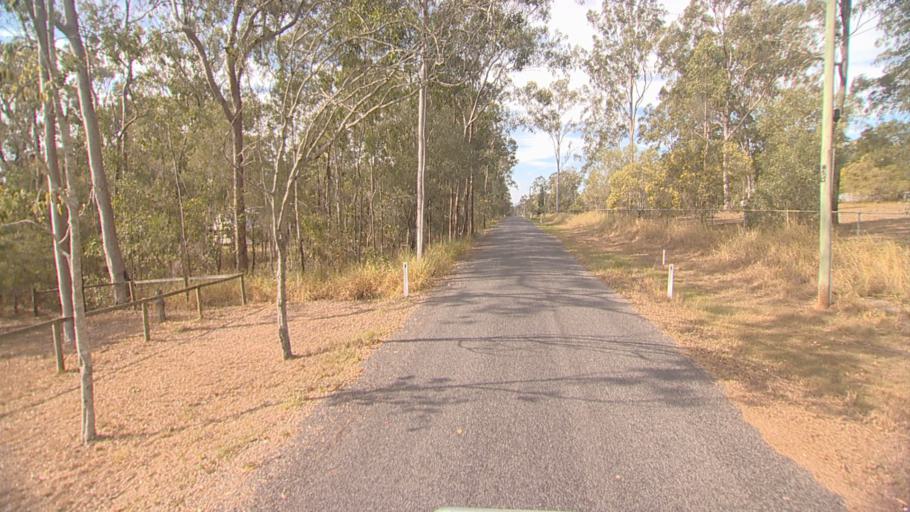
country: AU
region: Queensland
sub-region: Logan
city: North Maclean
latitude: -27.7648
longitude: 152.9679
